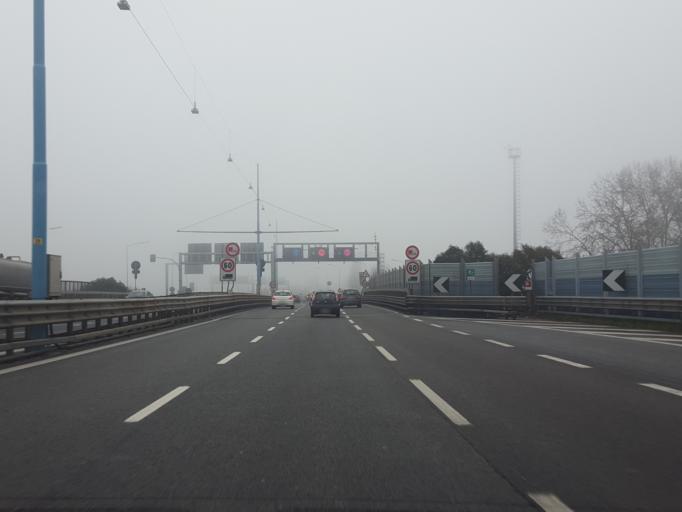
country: IT
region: Veneto
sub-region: Provincia di Venezia
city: Mestre
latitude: 45.4801
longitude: 12.2172
